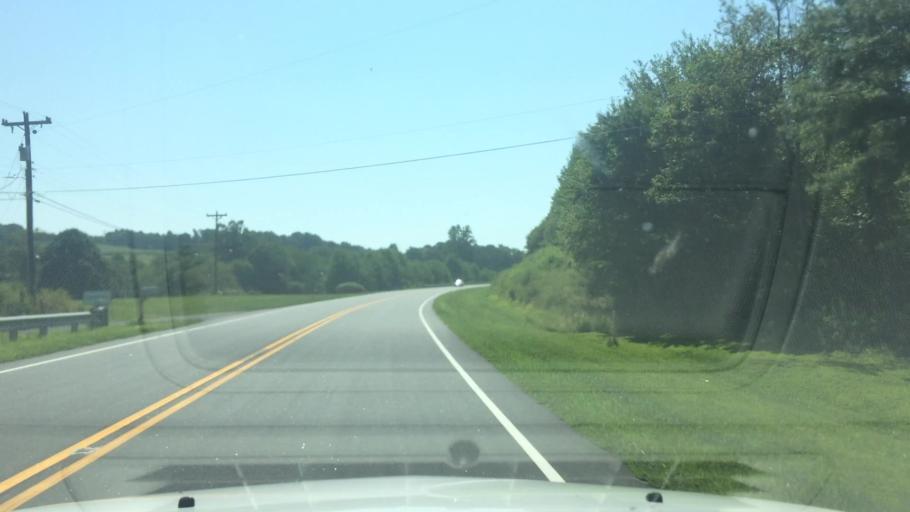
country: US
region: North Carolina
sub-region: Alexander County
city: Taylorsville
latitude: 35.9252
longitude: -81.2666
